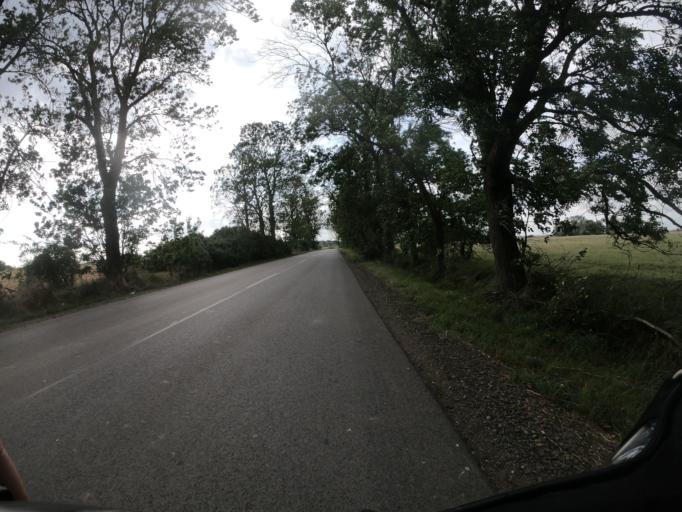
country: HU
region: Borsod-Abauj-Zemplen
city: Mezocsat
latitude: 47.8223
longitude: 20.8521
